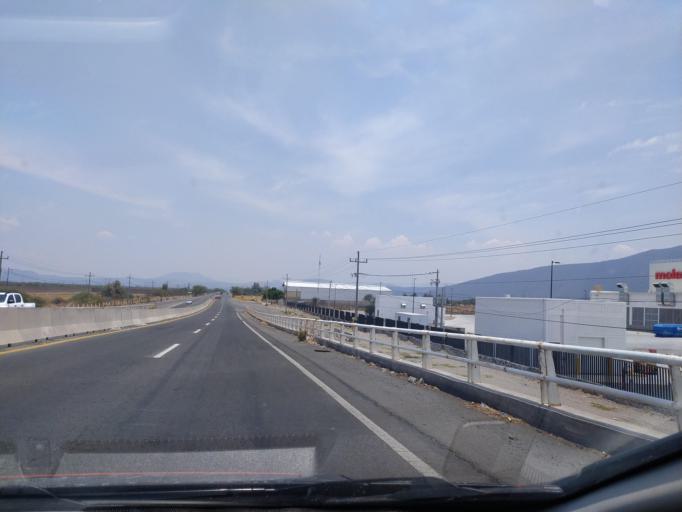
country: MX
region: Jalisco
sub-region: Acatlan de Juarez
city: Villa de los Ninos
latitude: 20.3444
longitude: -103.5912
